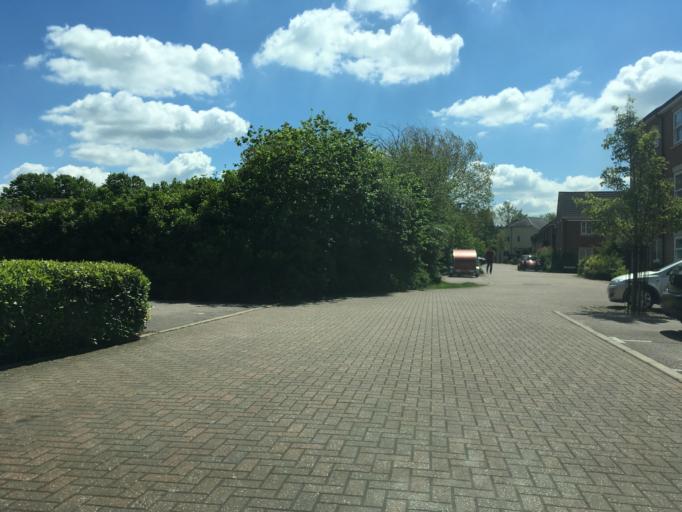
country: GB
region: England
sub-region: Milton Keynes
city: Woburn Sands
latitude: 52.0164
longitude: -0.6520
